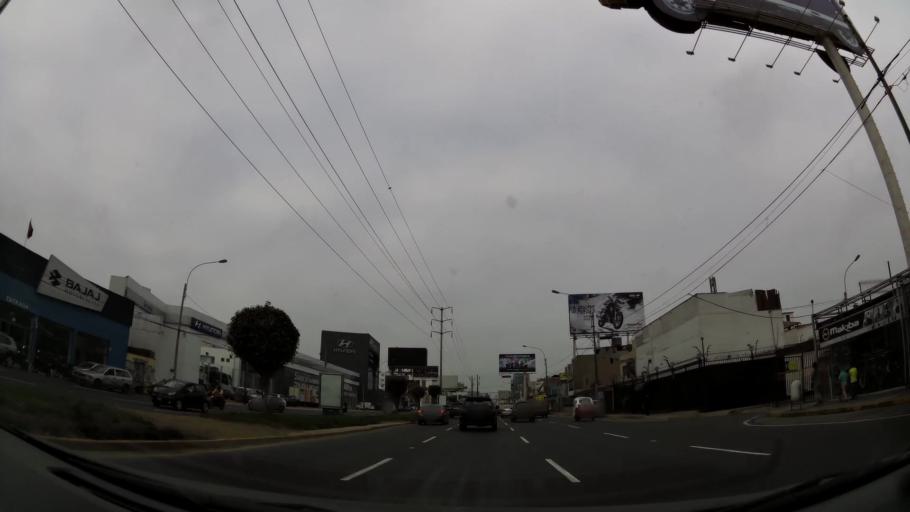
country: PE
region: Lima
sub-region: Lima
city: San Isidro
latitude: -12.0813
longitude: -77.0725
